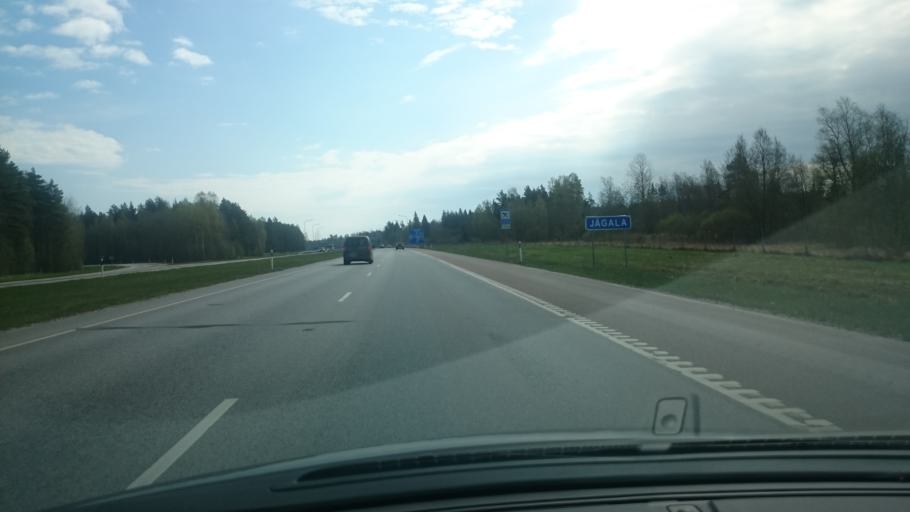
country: EE
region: Harju
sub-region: Raasiku vald
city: Raasiku
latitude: 59.4349
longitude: 25.1726
